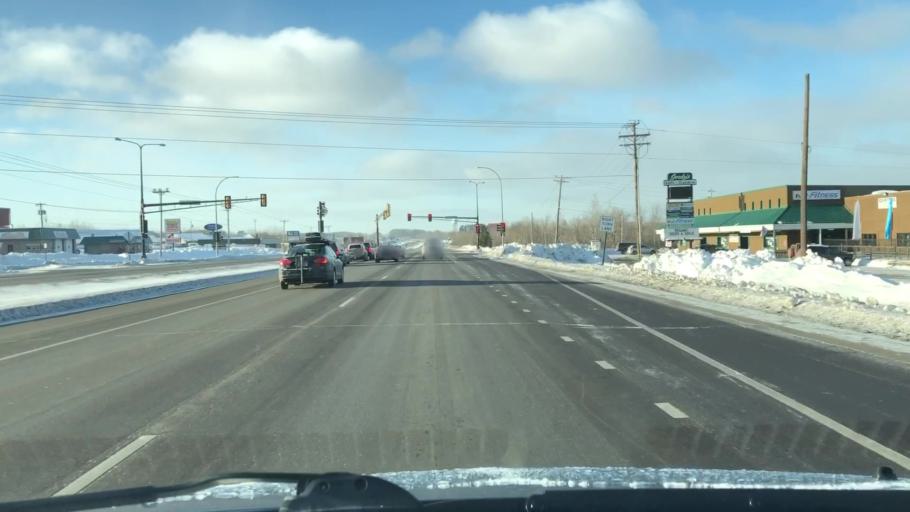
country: US
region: Minnesota
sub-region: Saint Louis County
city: Hermantown
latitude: 46.8270
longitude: -92.1946
